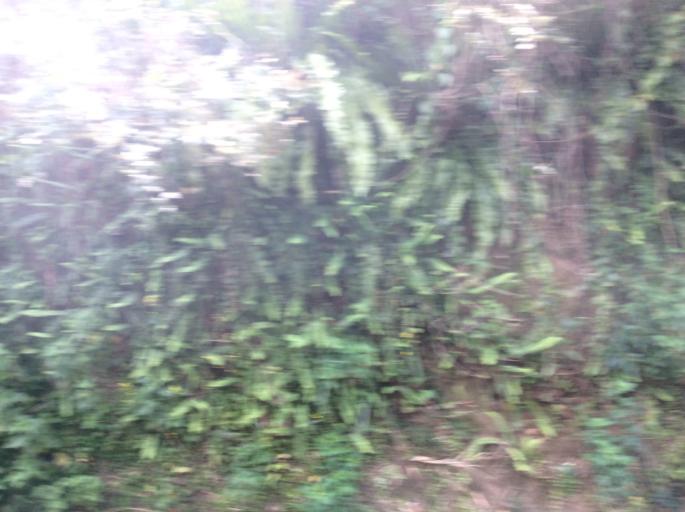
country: TW
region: Taipei
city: Taipei
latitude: 25.1406
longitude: 121.5491
